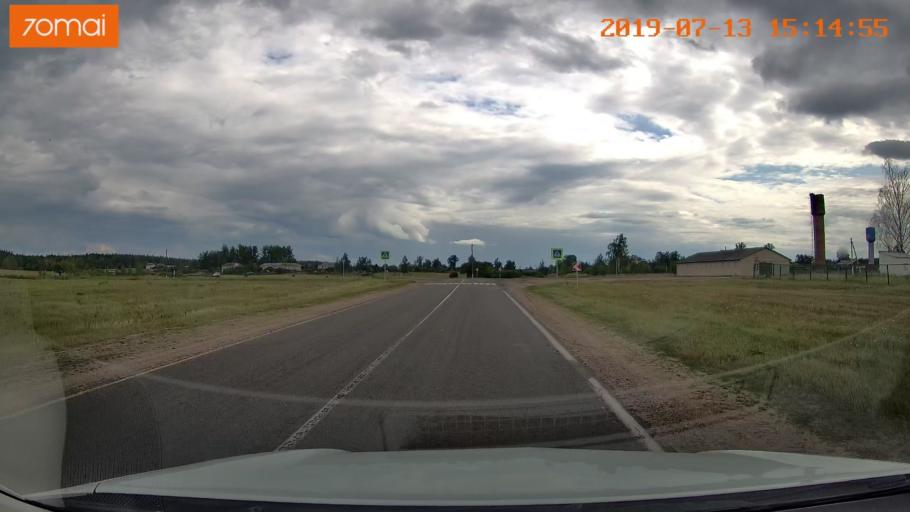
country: BY
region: Mogilev
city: Hlusha
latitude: 53.1207
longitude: 28.8213
